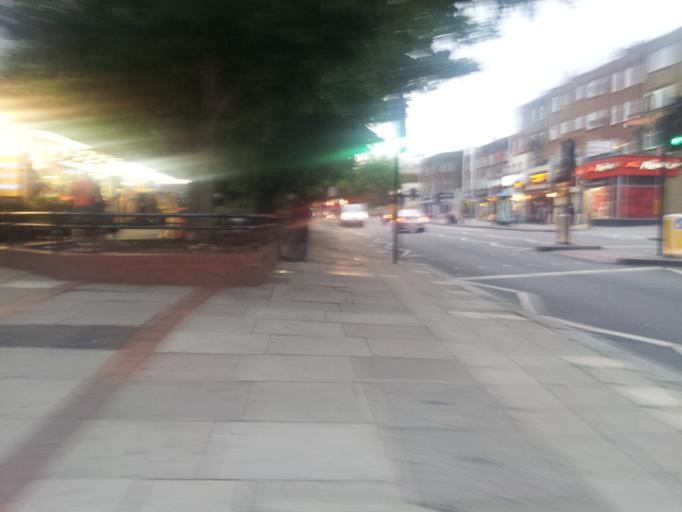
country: GB
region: England
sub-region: Greater London
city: Bayswater
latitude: 51.5230
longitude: -0.1746
